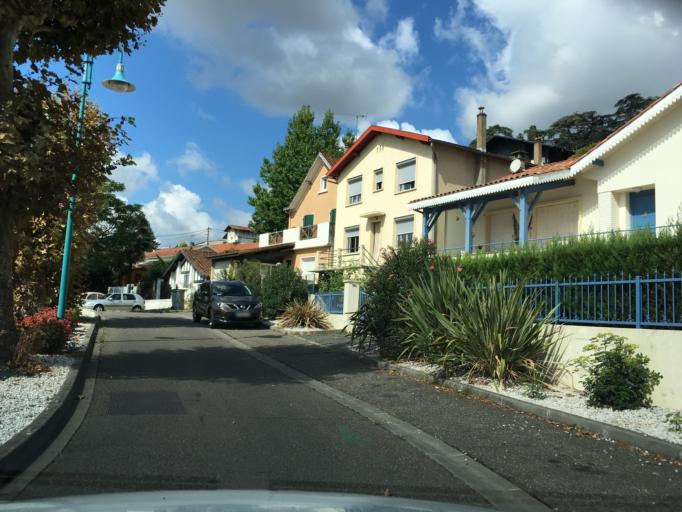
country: FR
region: Aquitaine
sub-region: Departement du Lot-et-Garonne
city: Agen
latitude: 44.2100
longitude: 0.6266
